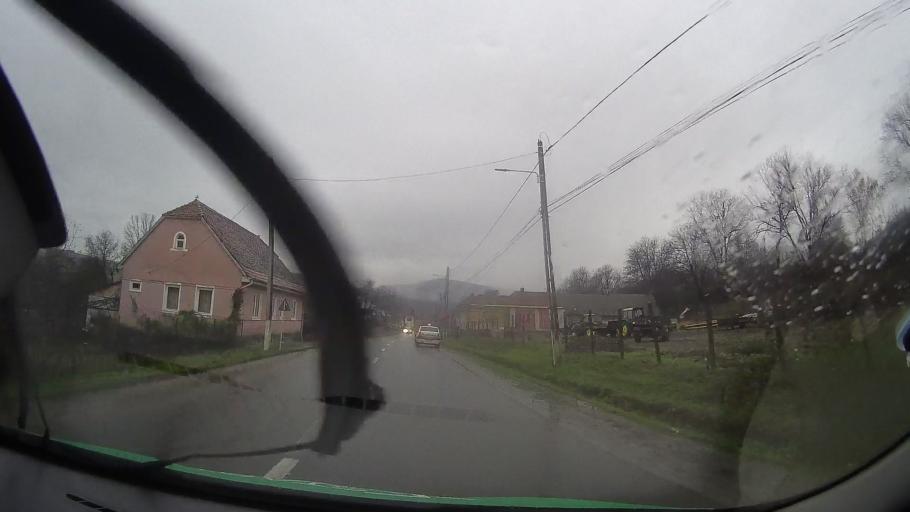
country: RO
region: Bistrita-Nasaud
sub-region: Comuna Sieut
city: Sieut
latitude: 46.9776
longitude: 24.6432
